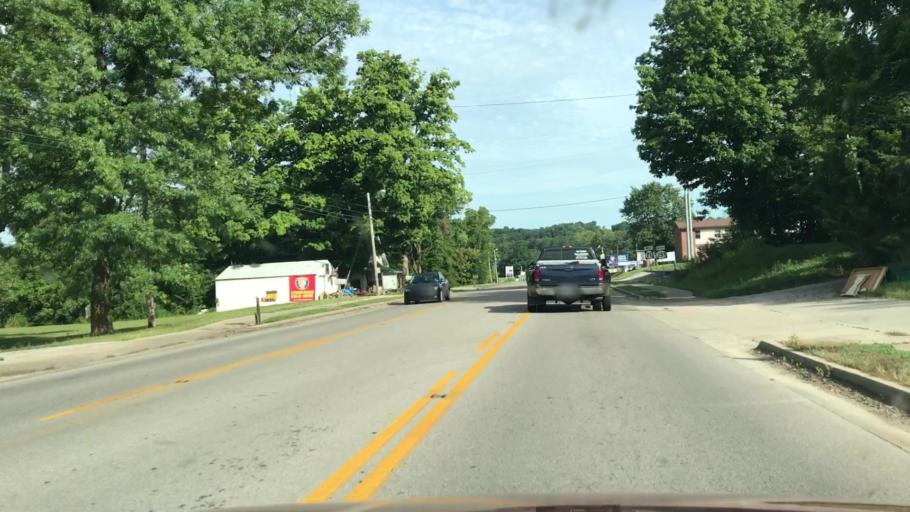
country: US
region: Kentucky
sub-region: Edmonson County
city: Brownsville
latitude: 37.1877
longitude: -86.2525
